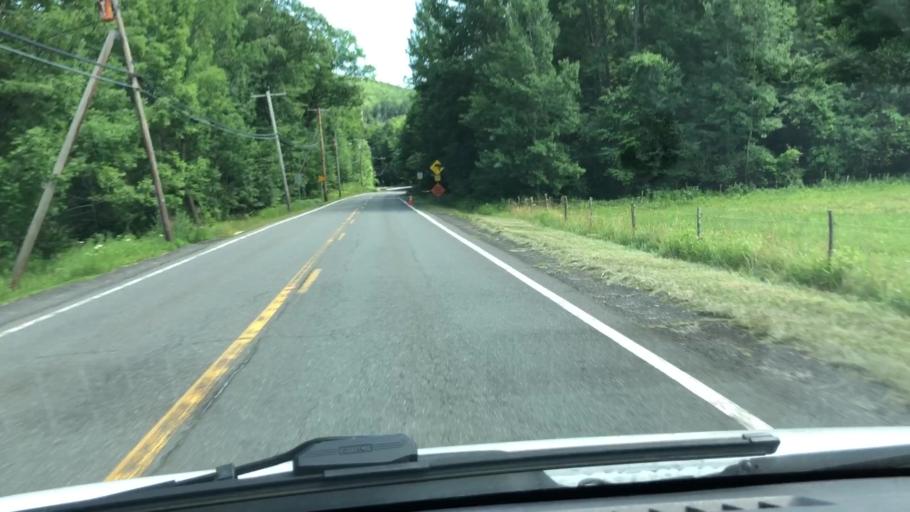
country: US
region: Massachusetts
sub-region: Hampshire County
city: Williamsburg
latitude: 42.4210
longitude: -72.7769
